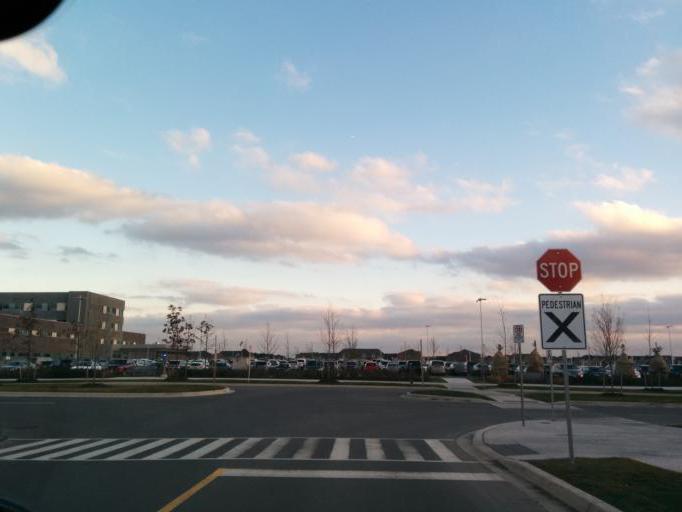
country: CA
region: Ontario
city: Oakville
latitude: 43.4500
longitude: -79.7660
